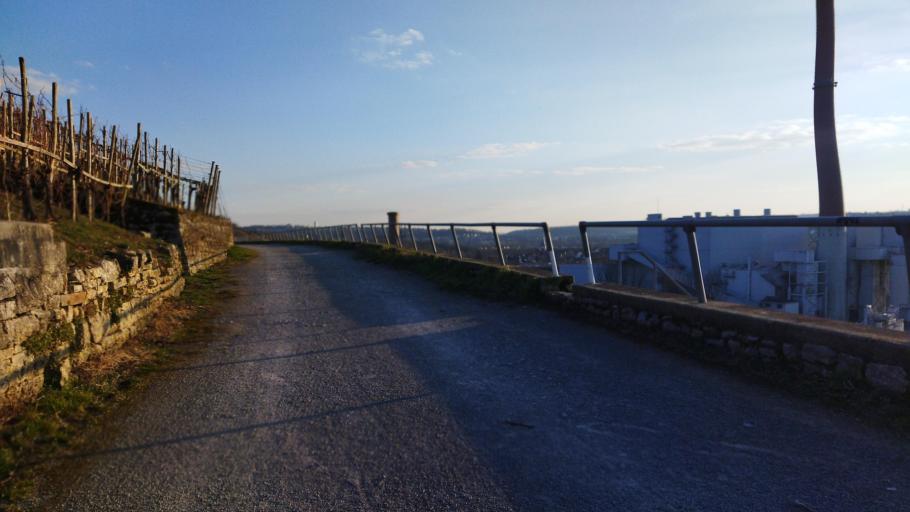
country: DE
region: Baden-Wuerttemberg
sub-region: Regierungsbezirk Stuttgart
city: Gemmrigheim
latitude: 49.0205
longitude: 9.1598
